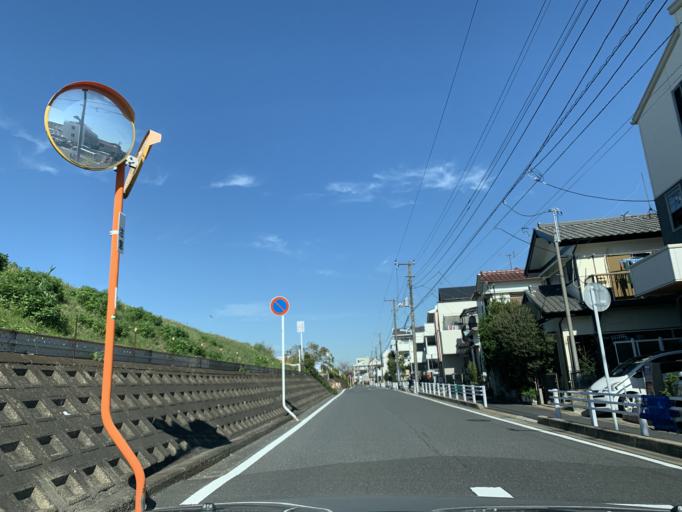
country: JP
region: Tokyo
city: Urayasu
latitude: 35.6522
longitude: 139.8875
